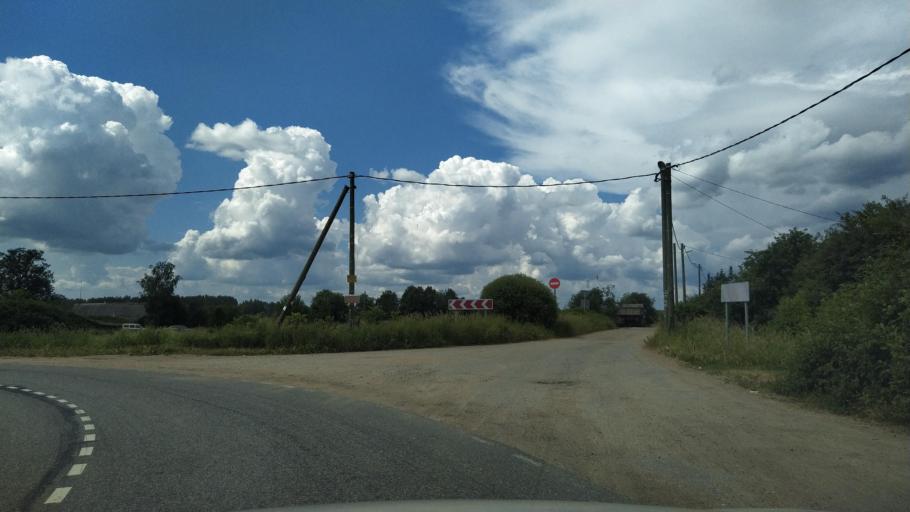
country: RU
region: Leningrad
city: Rozhdestveno
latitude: 59.3468
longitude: 29.9511
